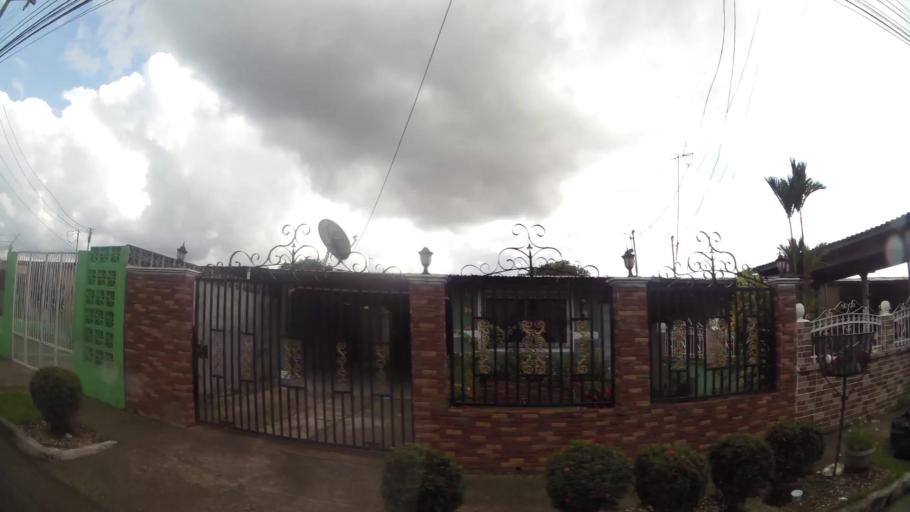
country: PA
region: Panama
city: Nuevo Arraijan
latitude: 8.9341
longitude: -79.7390
